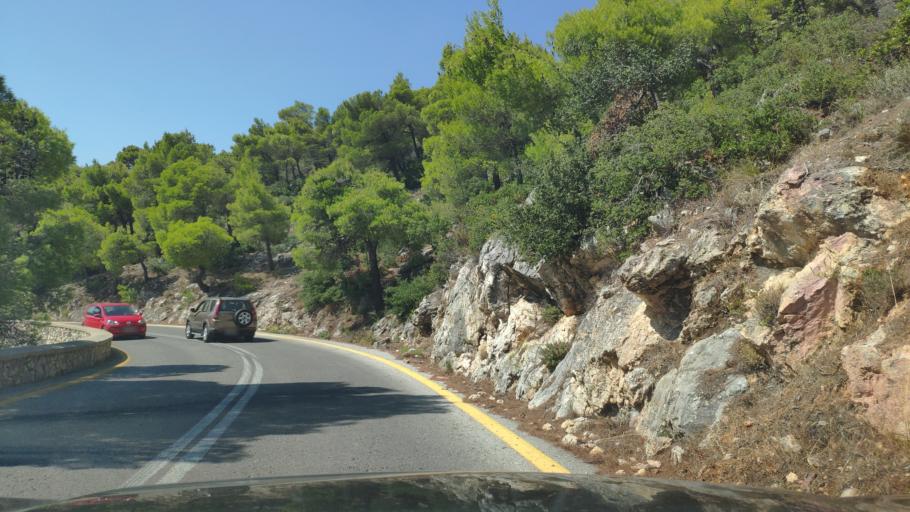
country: GR
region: Attica
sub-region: Nomarchia Anatolikis Attikis
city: Thrakomakedones
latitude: 38.1400
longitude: 23.7294
